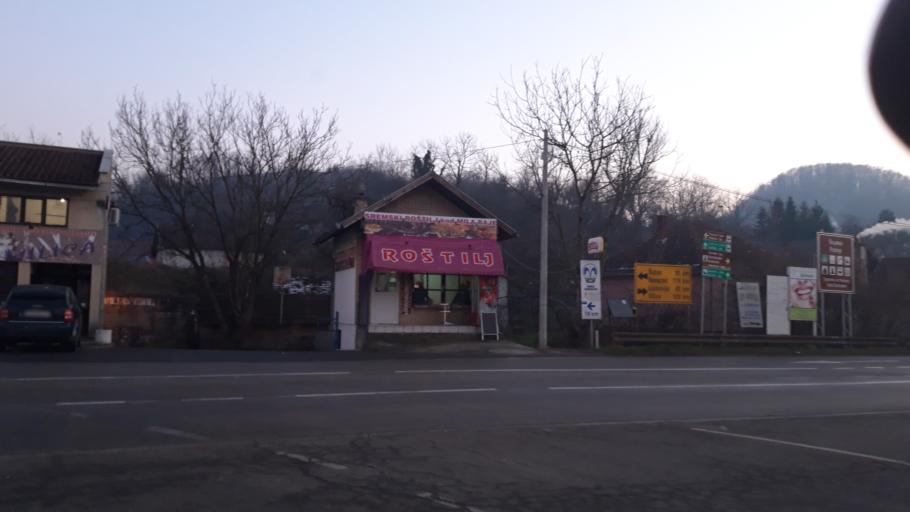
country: BA
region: Republika Srpska
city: Zvornik
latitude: 44.4033
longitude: 19.1261
